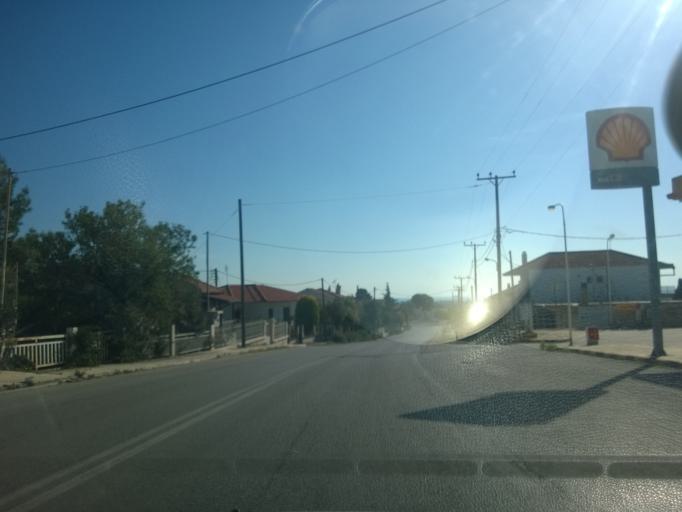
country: GR
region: Central Macedonia
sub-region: Nomos Chalkidikis
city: Nea Kallikrateia
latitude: 40.3428
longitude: 23.0602
